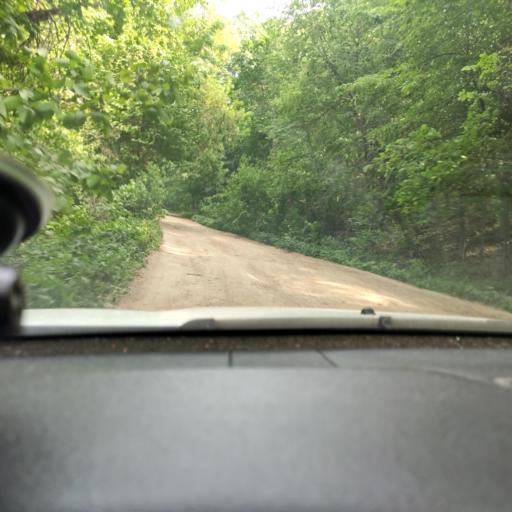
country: RU
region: Samara
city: Novosemeykino
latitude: 53.3373
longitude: 50.2210
